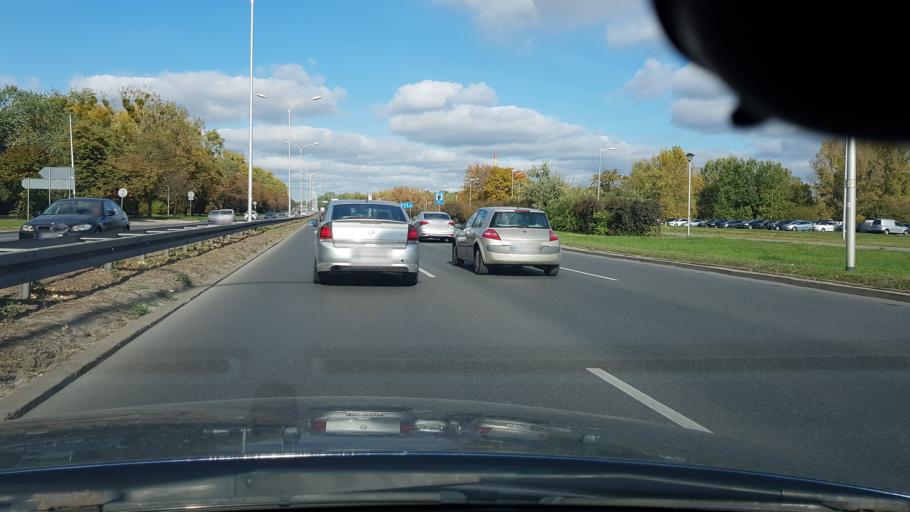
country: PL
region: Masovian Voivodeship
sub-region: Warszawa
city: Zoliborz
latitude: 52.2747
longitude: 20.9953
